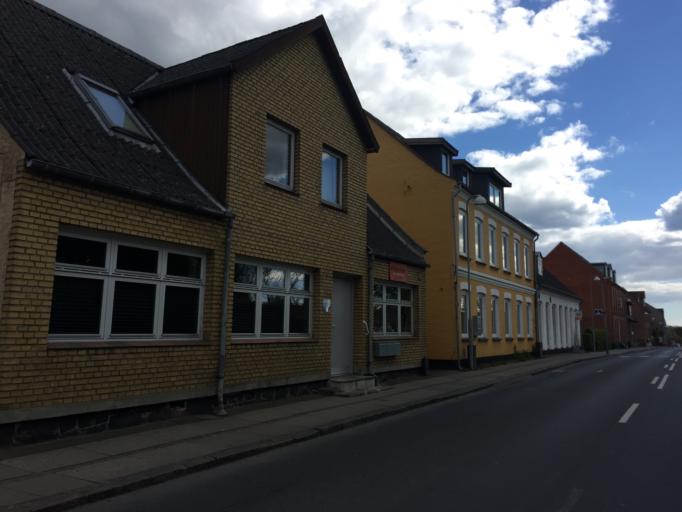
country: DK
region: Zealand
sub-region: Slagelse Kommune
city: Skaelskor
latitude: 55.2541
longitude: 11.2979
